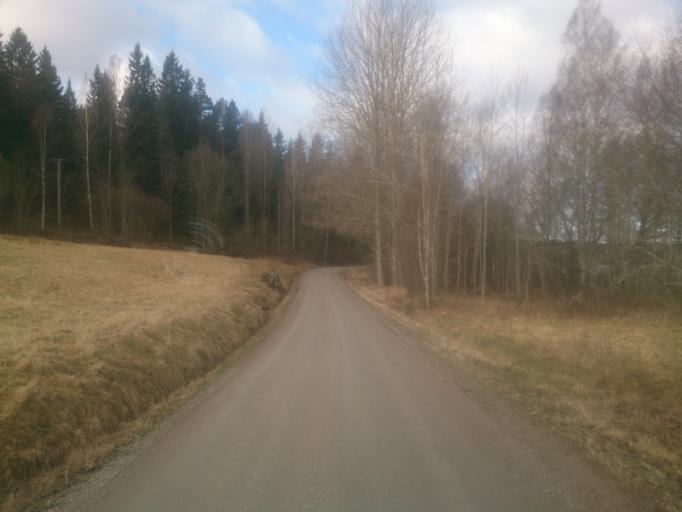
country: SE
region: OEstergoetland
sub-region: Atvidabergs Kommun
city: Atvidaberg
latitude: 58.2063
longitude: 16.1637
